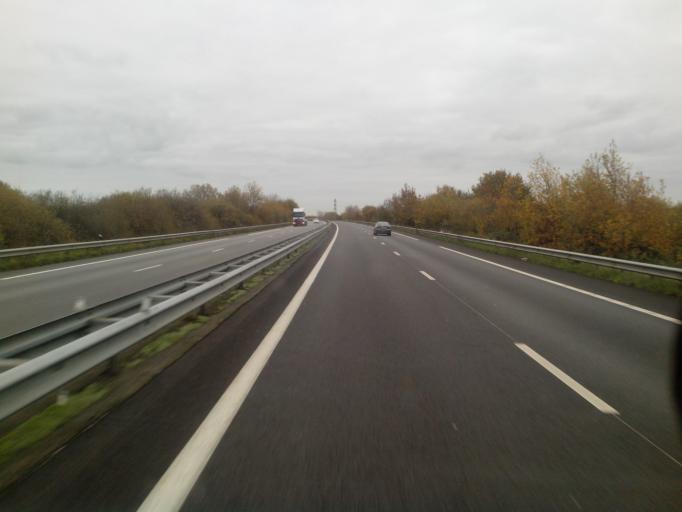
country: FR
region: Pays de la Loire
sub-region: Departement de la Loire-Atlantique
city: Derval
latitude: 47.6577
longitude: -1.6754
